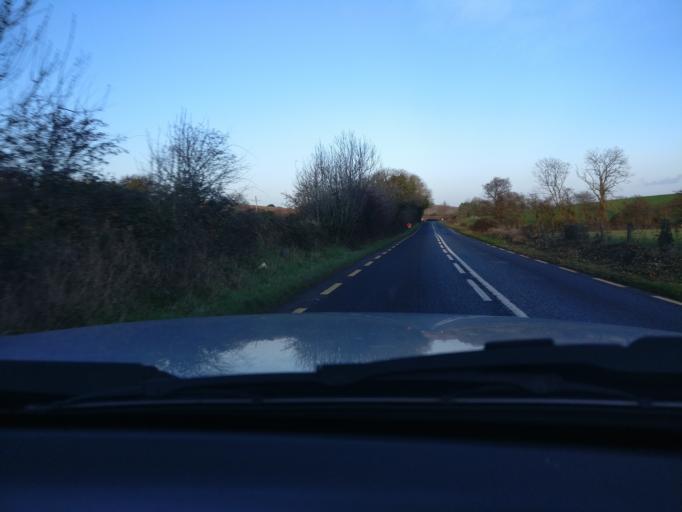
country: IE
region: Leinster
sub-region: Lu
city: Ardee
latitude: 53.8320
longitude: -6.6255
